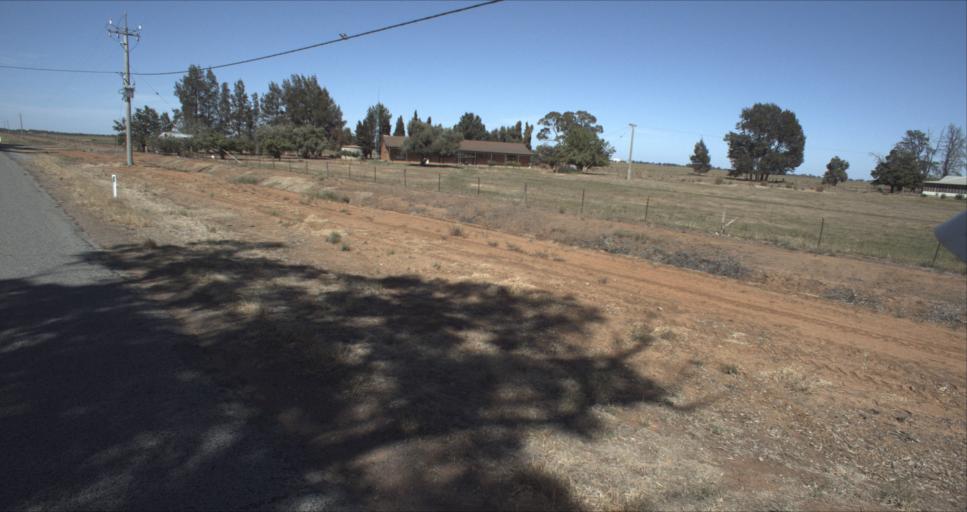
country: AU
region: New South Wales
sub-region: Leeton
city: Leeton
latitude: -34.5439
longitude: 146.3160
